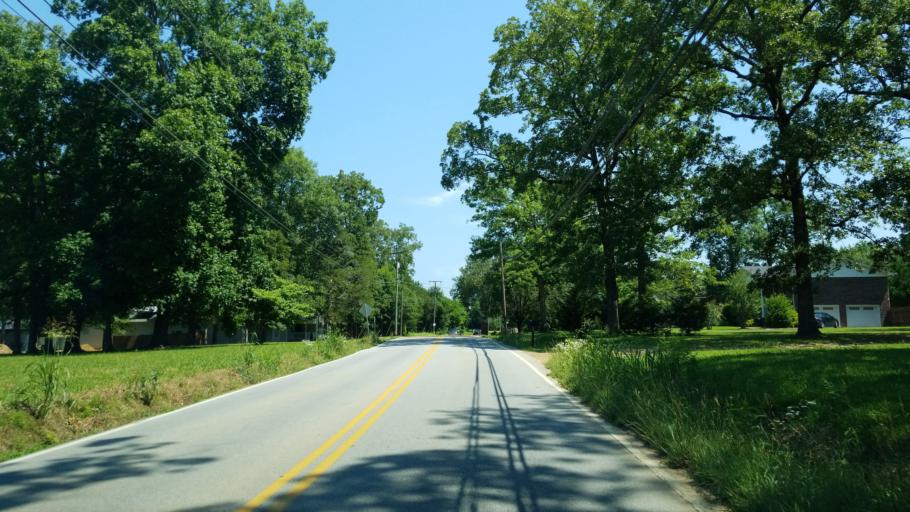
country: US
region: Tennessee
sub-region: Hamilton County
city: Collegedale
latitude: 35.0974
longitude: -85.0516
